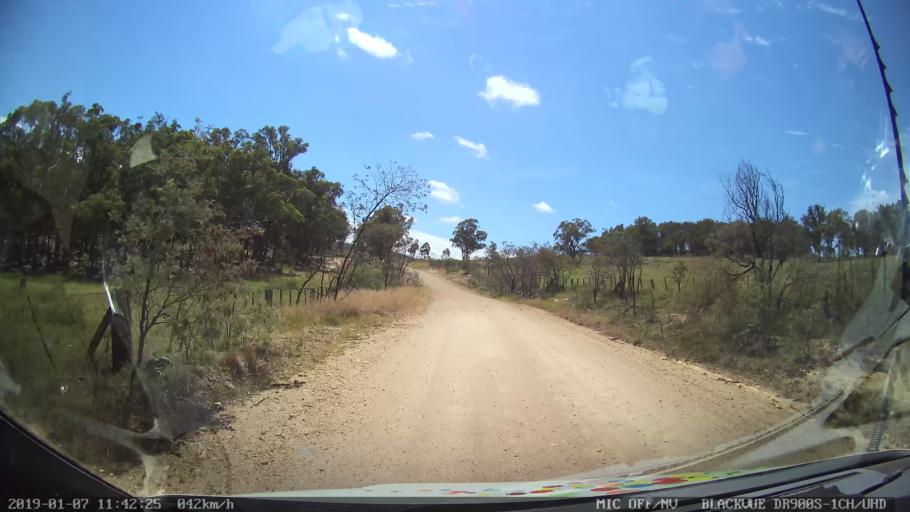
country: AU
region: New South Wales
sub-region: Guyra
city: Guyra
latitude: -30.3581
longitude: 151.5941
